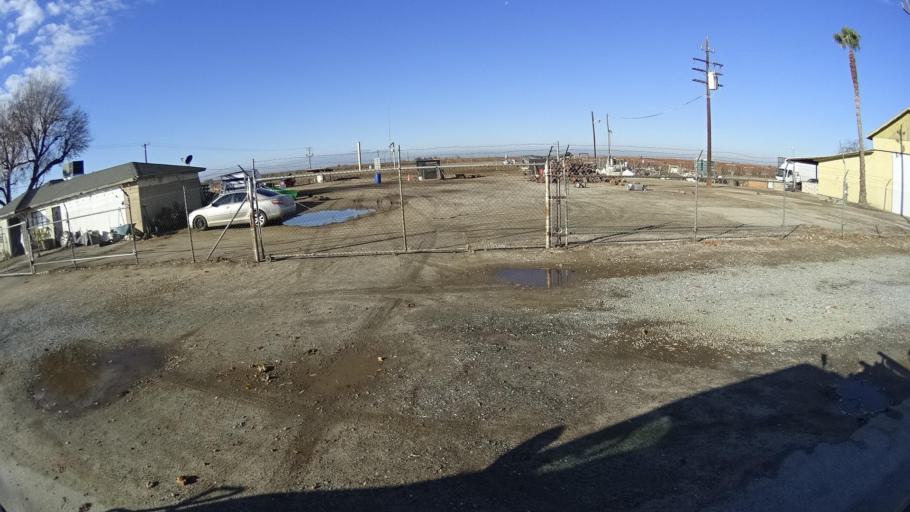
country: US
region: California
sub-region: Kern County
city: Delano
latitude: 35.7184
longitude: -119.2941
